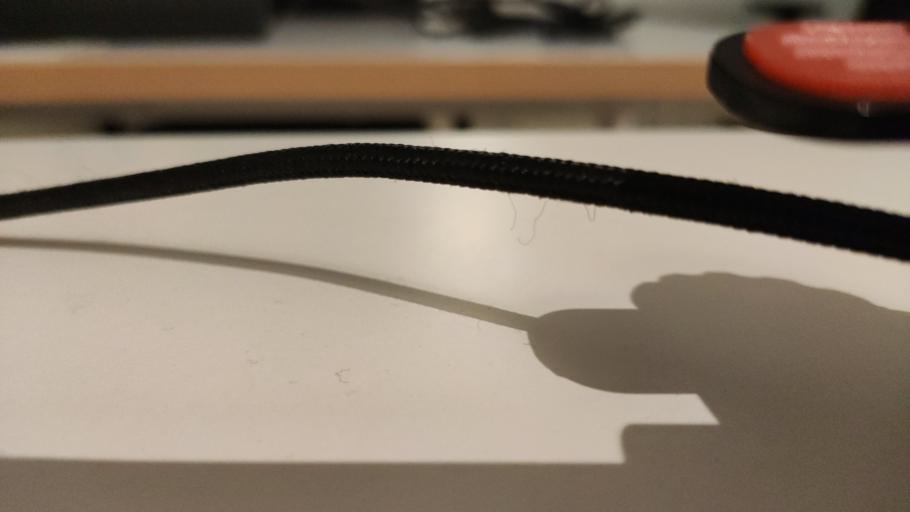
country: RU
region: Moskovskaya
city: Novosin'kovo
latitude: 56.3957
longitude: 37.2745
